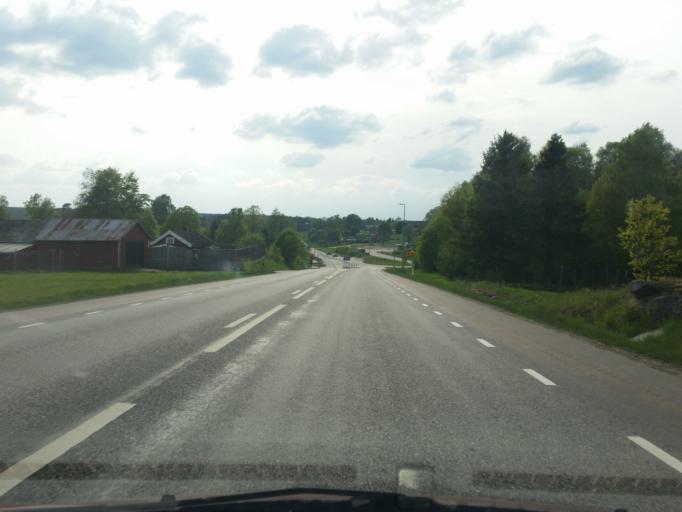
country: SE
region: Vaestra Goetaland
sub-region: Ulricehamns Kommun
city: Ulricehamn
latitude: 57.8091
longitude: 13.2605
